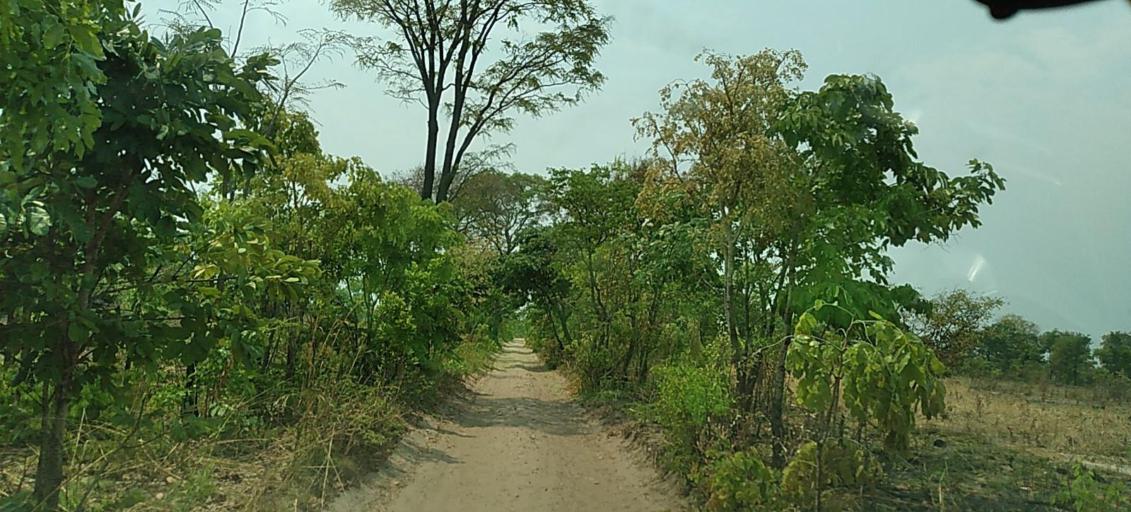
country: ZM
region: North-Western
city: Kabompo
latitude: -13.4675
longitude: 24.4400
